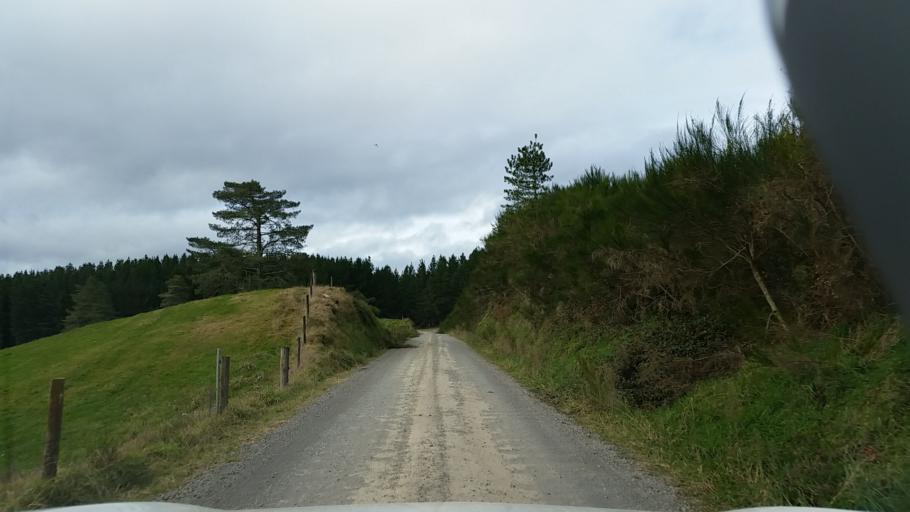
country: NZ
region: Bay of Plenty
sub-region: Whakatane District
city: Murupara
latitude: -38.3432
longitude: 176.5421
